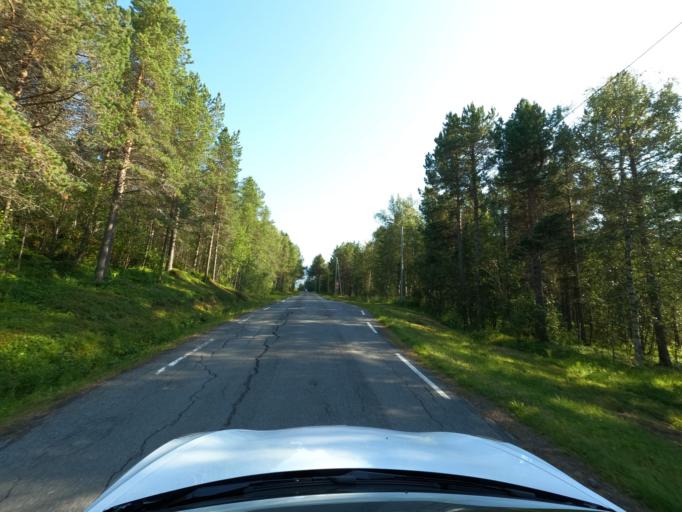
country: NO
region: Nordland
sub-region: Narvik
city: Bjerkvik
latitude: 68.4801
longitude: 17.5277
